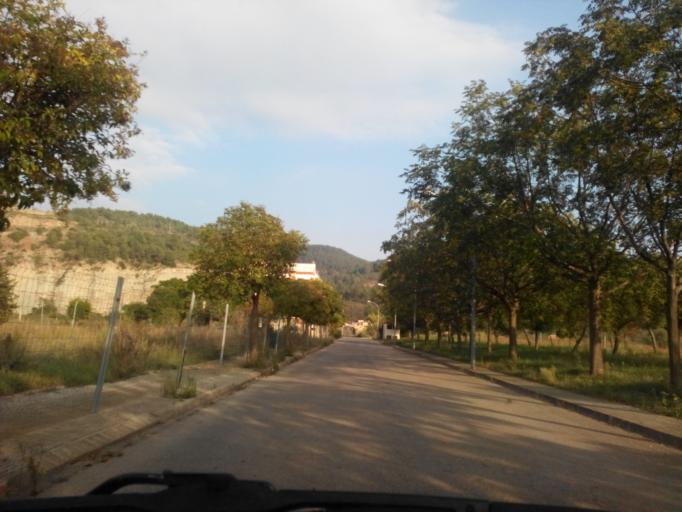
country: ES
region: Catalonia
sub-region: Provincia de Barcelona
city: Sallent
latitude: 41.8156
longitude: 1.8975
